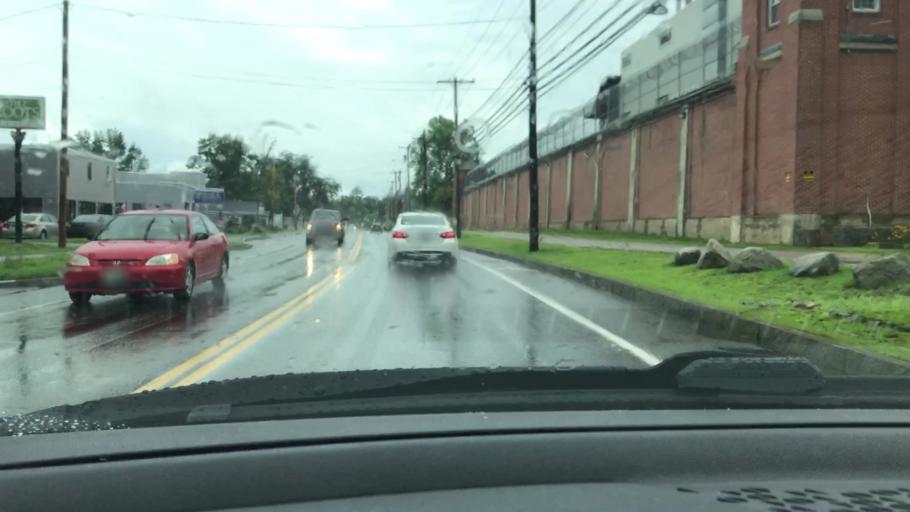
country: US
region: New Hampshire
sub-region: Merrimack County
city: East Concord
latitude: 43.2289
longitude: -71.5584
